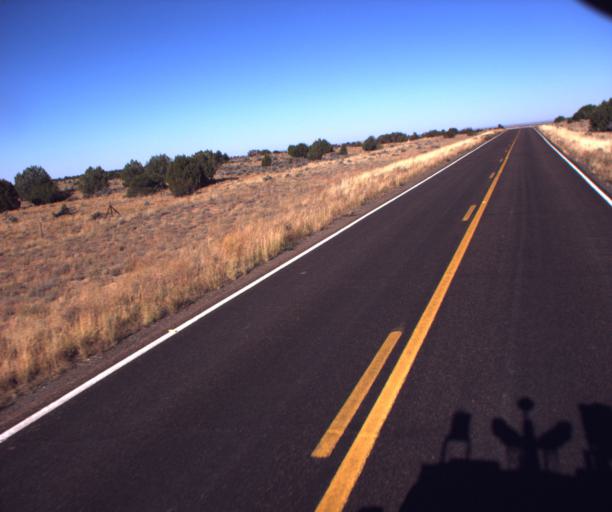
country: US
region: Arizona
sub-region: Navajo County
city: First Mesa
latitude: 35.7928
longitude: -110.1859
